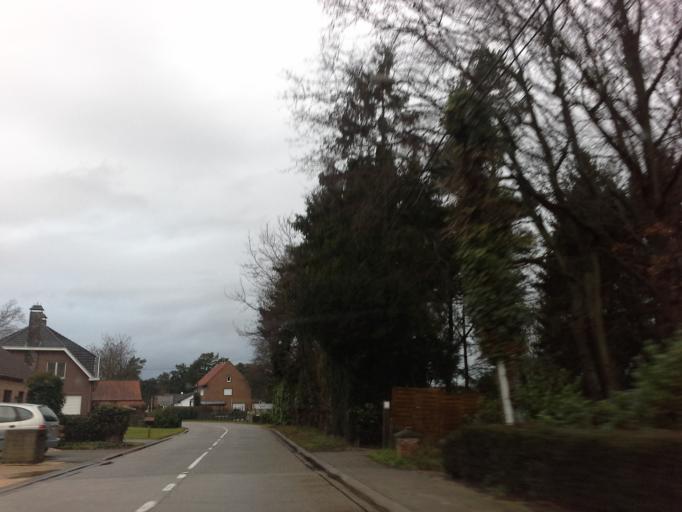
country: BE
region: Flanders
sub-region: Provincie Antwerpen
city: Meerhout
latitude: 51.1382
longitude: 5.0711
